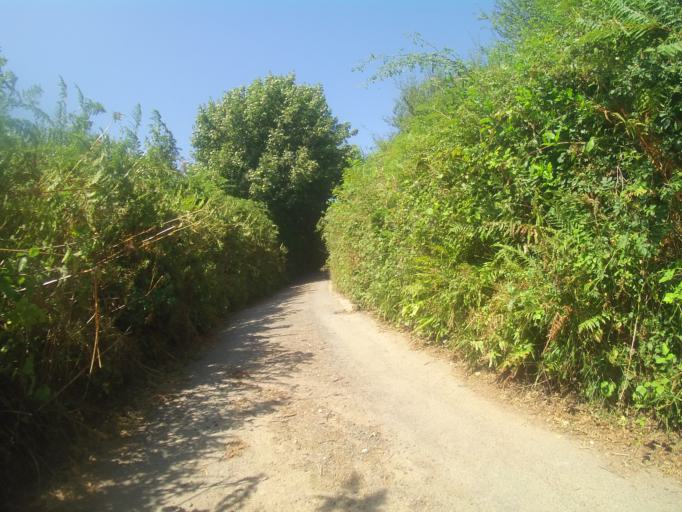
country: GB
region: England
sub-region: Devon
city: Dartmouth
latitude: 50.3634
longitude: -3.6229
